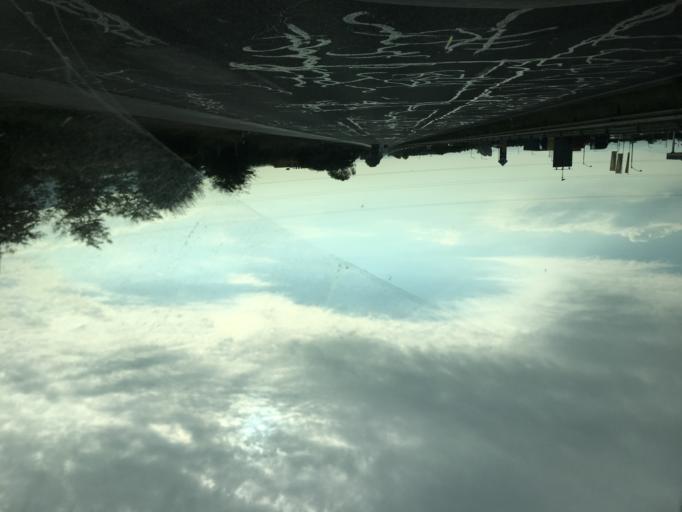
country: BG
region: Sofiya
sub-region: Obshtina Elin Pelin
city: Elin Pelin
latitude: 42.6319
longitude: 23.4573
